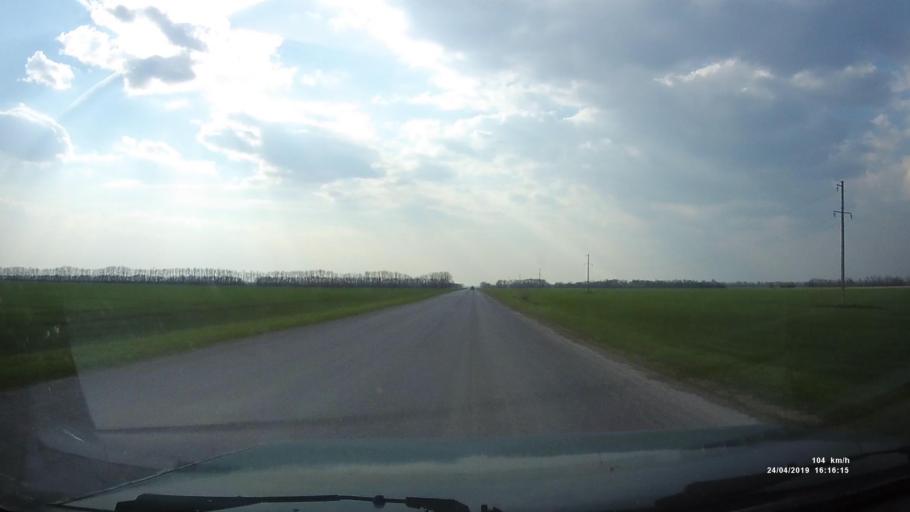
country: RU
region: Rostov
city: Sovetskoye
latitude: 46.7621
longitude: 42.1637
